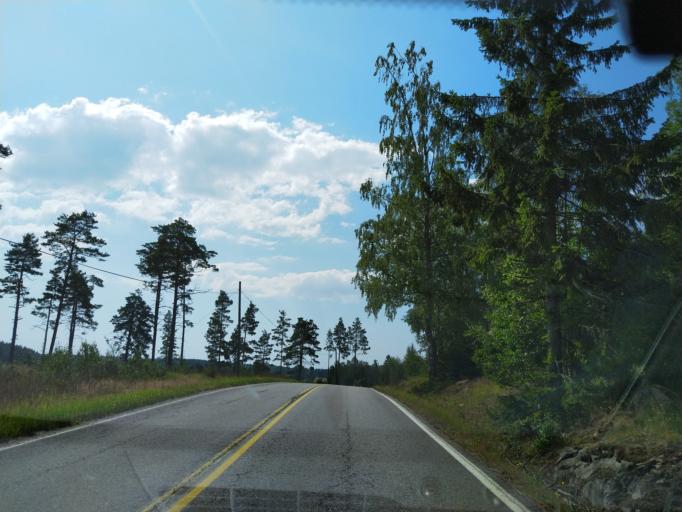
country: FI
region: Uusimaa
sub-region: Helsinki
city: Kirkkonummi
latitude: 60.0211
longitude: 24.4793
